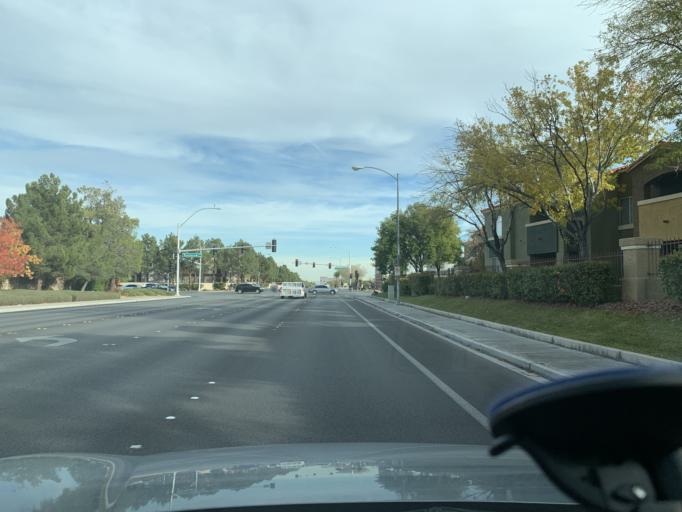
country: US
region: Nevada
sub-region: Clark County
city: Spring Valley
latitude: 36.0924
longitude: -115.2440
